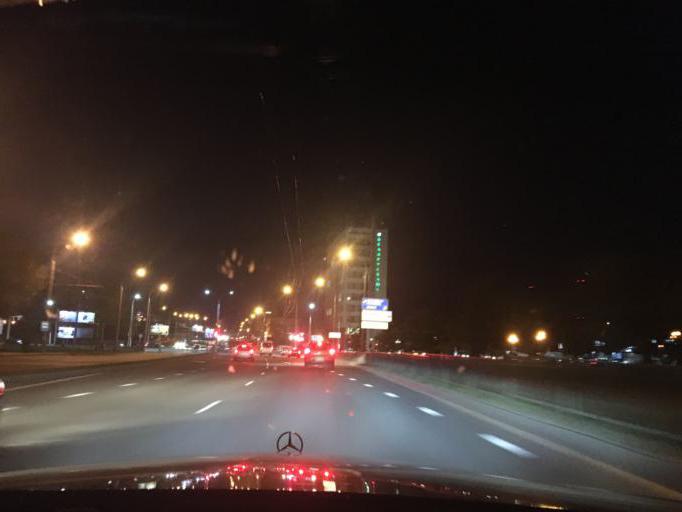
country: BY
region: Brest
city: Brest
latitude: 52.0920
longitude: 23.7331
